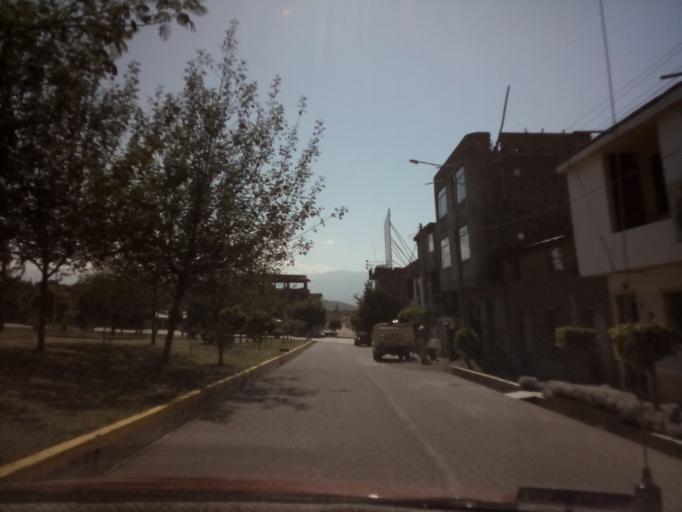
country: PE
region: Ayacucho
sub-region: Provincia de Huamanga
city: Ayacucho
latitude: -13.1450
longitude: -74.2267
